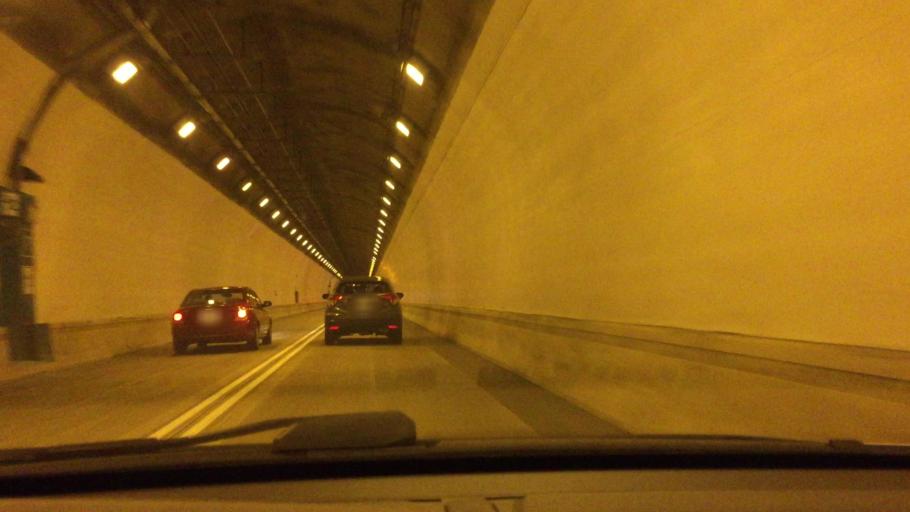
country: US
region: Pennsylvania
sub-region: Allegheny County
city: Mount Oliver
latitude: 40.4205
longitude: -80.0052
